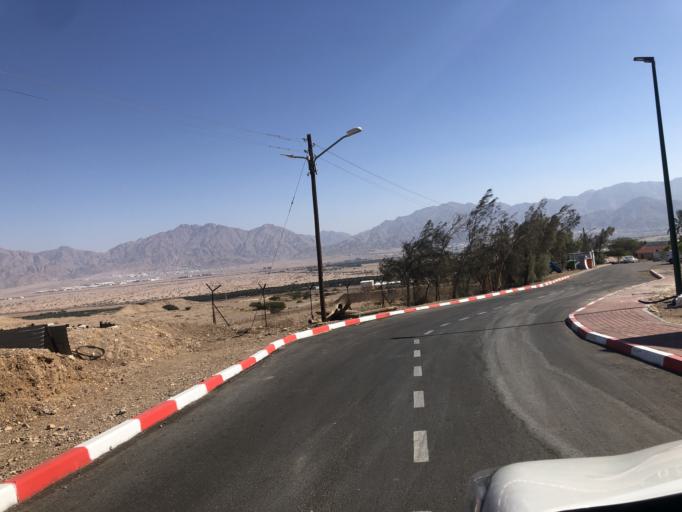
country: IL
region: Southern District
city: Eilat
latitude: 29.5833
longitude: 34.9623
